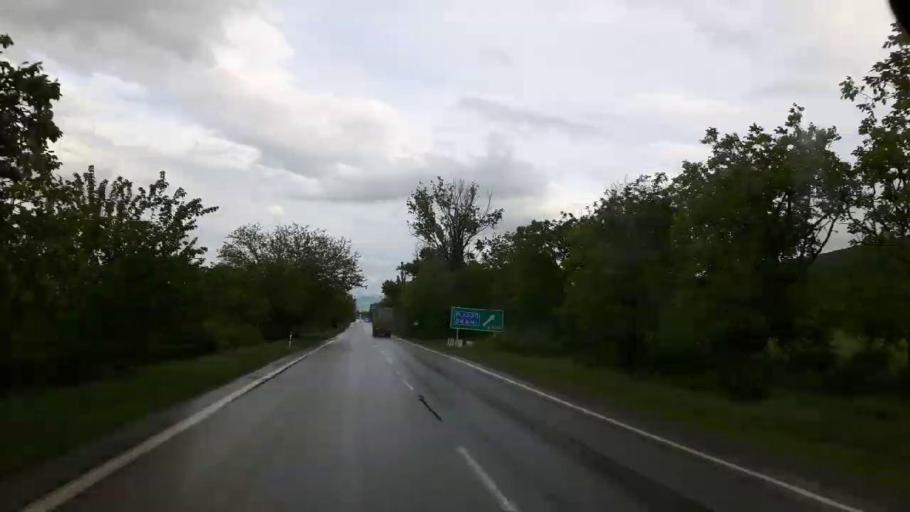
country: GE
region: Shida Kartli
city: Kaspi
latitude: 41.9678
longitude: 44.4607
